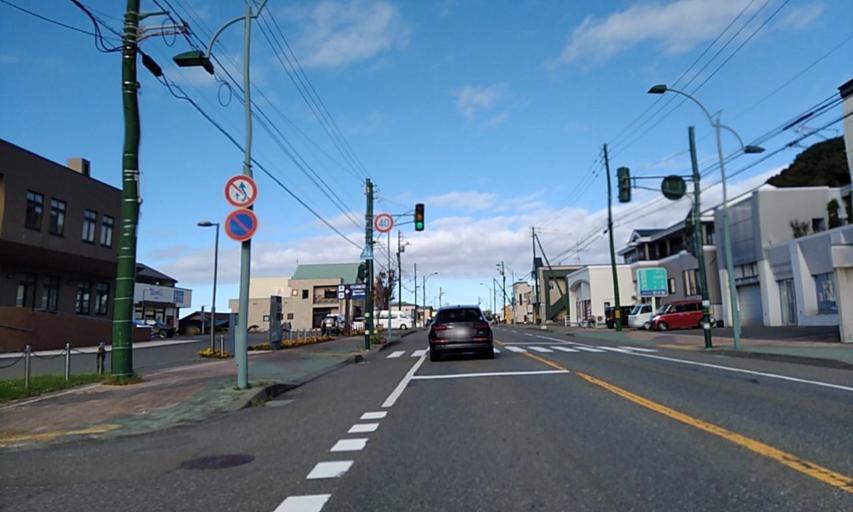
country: JP
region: Hokkaido
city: Shizunai-furukawacho
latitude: 42.2486
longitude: 142.5570
